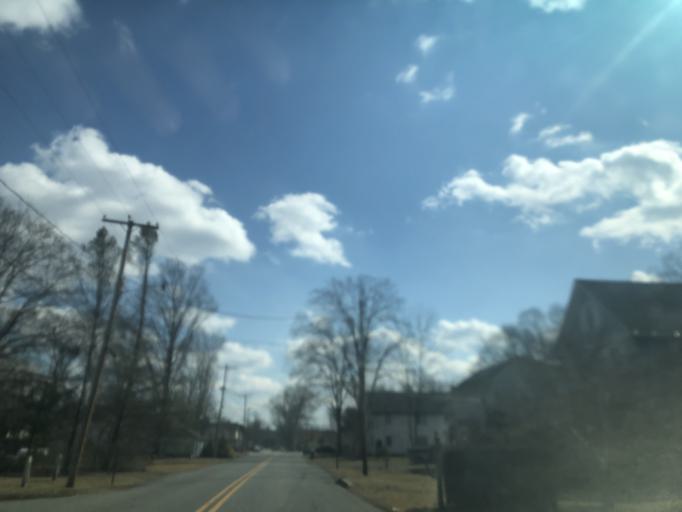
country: US
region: New Jersey
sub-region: Warren County
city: Belvidere
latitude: 40.9278
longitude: -75.0952
